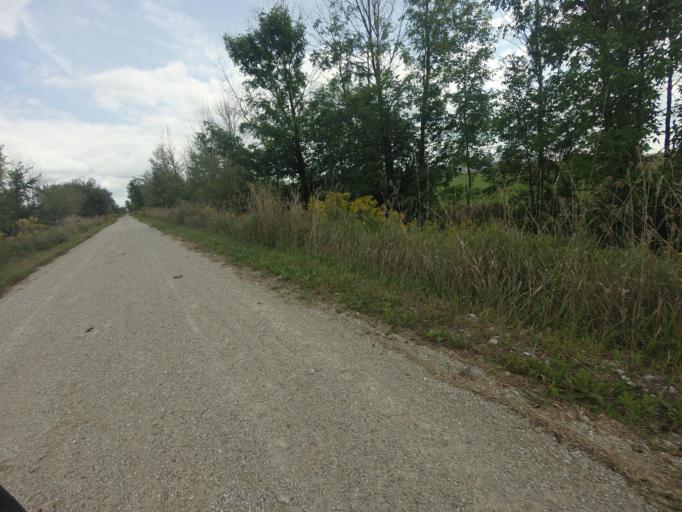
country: CA
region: Ontario
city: North Perth
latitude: 43.5717
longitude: -80.8701
